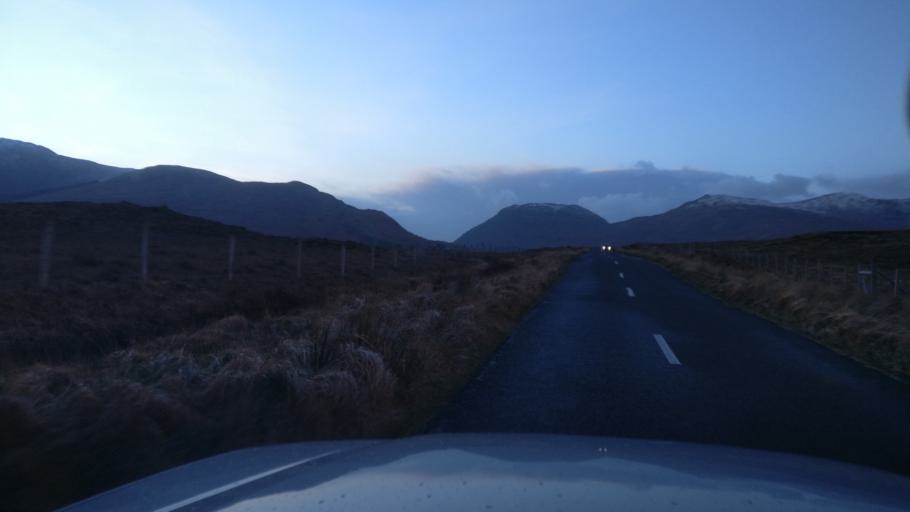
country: IE
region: Connaught
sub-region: County Galway
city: Clifden
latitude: 53.5510
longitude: -9.7985
